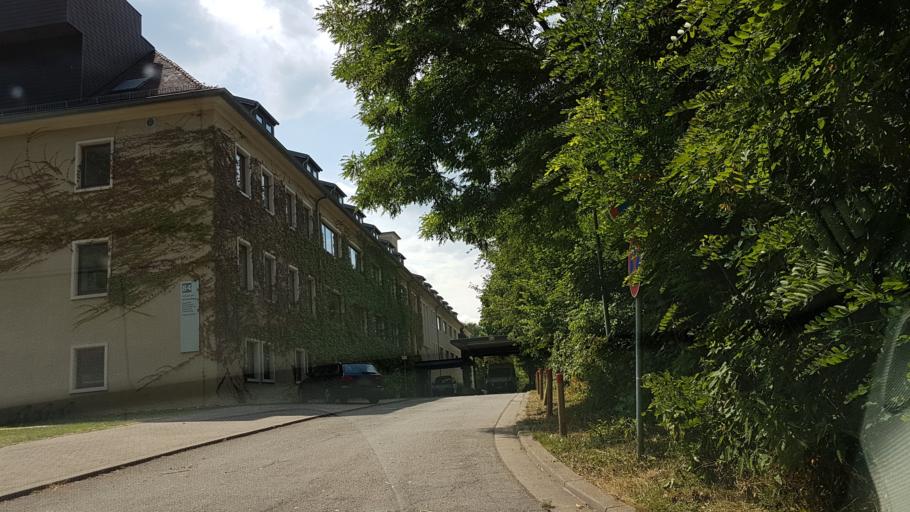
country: DE
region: Saarland
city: Homburg
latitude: 49.3034
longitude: 7.3411
